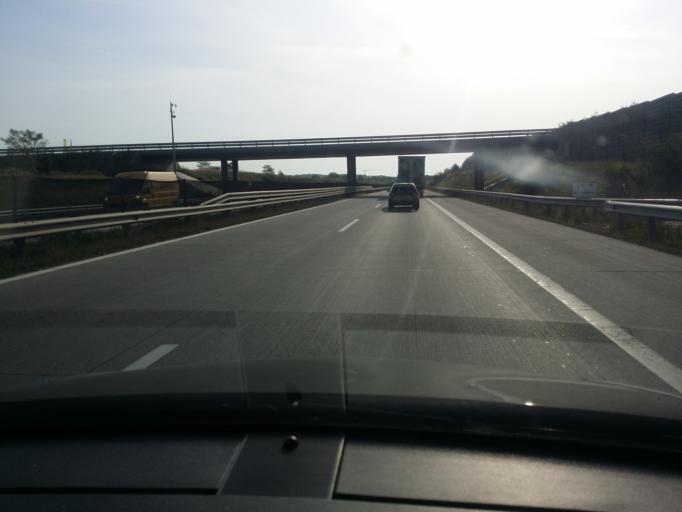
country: HU
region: Pest
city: Csomor
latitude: 47.5461
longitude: 19.1985
